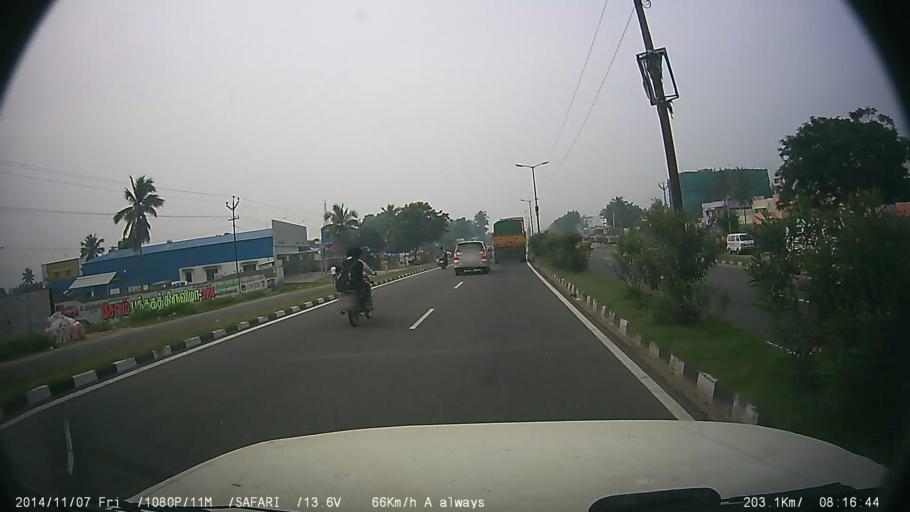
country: IN
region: Tamil Nadu
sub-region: Salem
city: Salem
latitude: 11.6720
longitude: 78.1275
